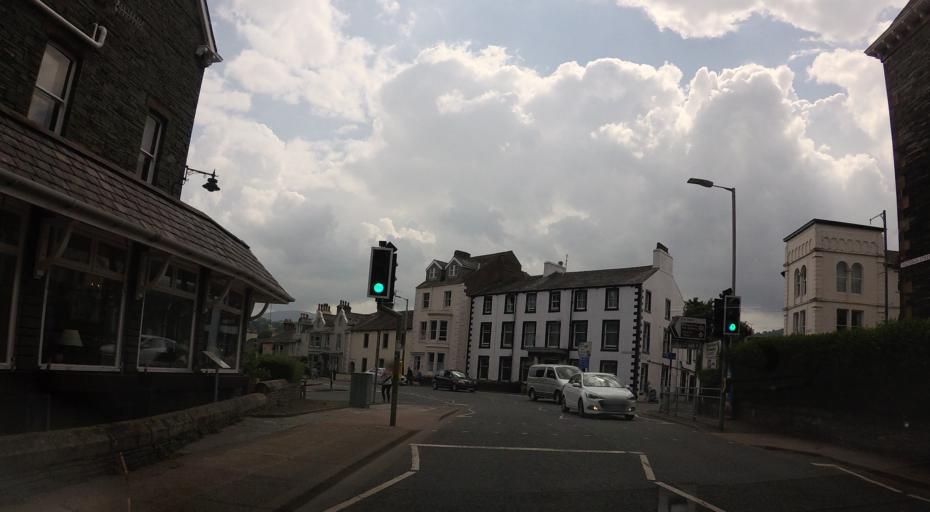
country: GB
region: England
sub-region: Cumbria
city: Keswick
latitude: 54.6013
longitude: -3.1349
